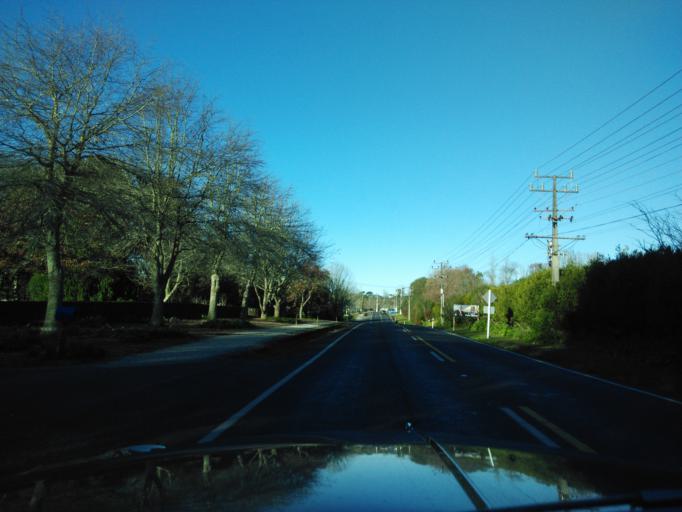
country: NZ
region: Auckland
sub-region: Auckland
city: Rothesay Bay
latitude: -36.7166
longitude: 174.6356
